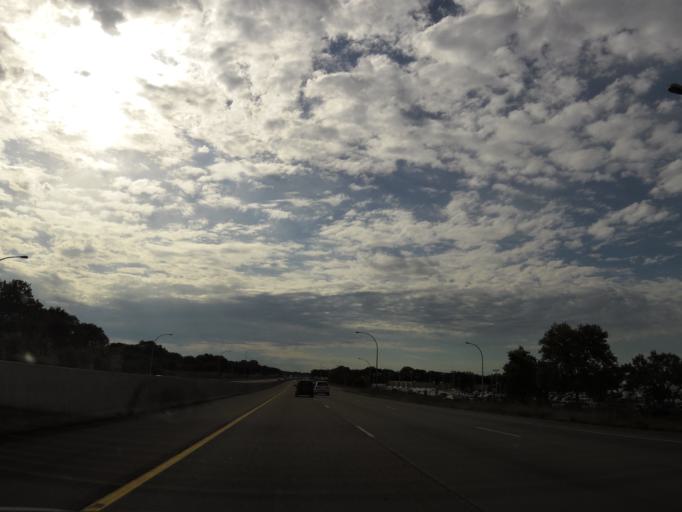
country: US
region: Minnesota
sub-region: Hennepin County
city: Brooklyn Center
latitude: 45.0760
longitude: -93.3344
